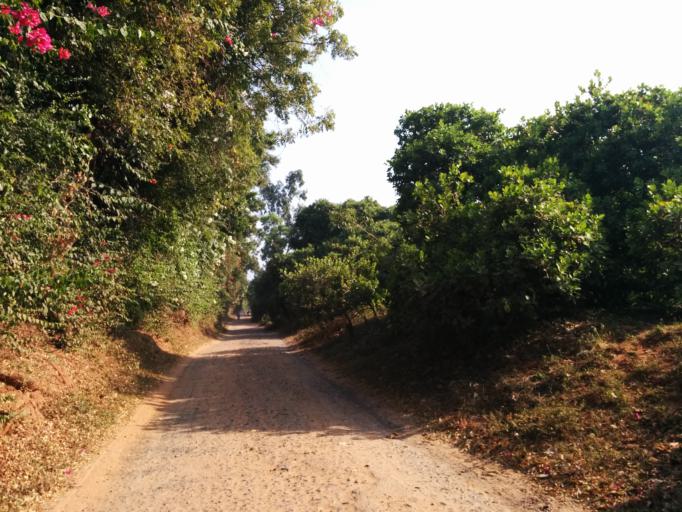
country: IN
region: Tamil Nadu
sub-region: Villupuram
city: Auroville
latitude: 11.9860
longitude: 79.8329
